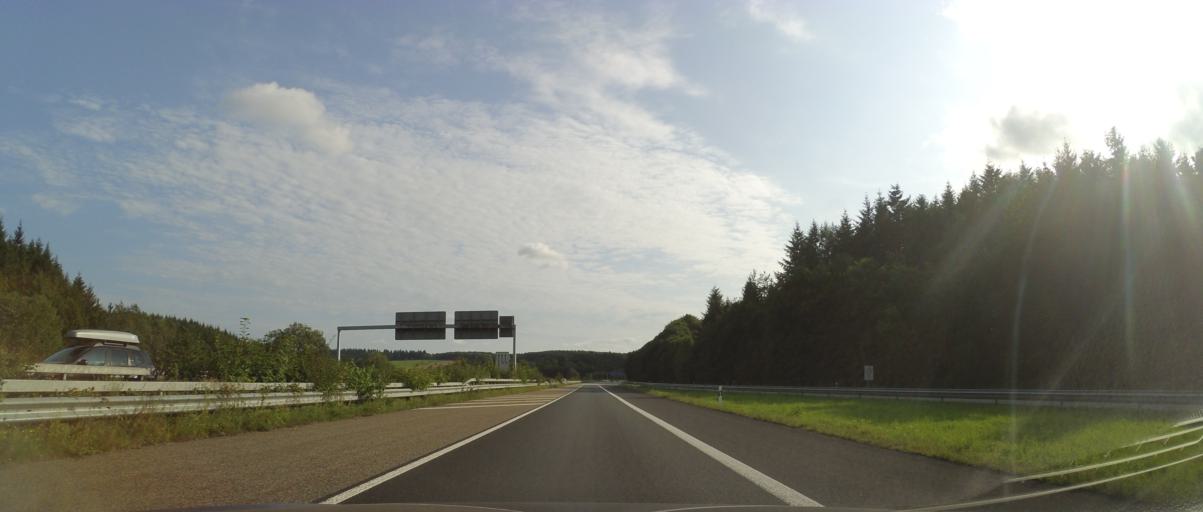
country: DE
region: Rheinland-Pfalz
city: Mehren
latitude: 50.1764
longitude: 6.8961
